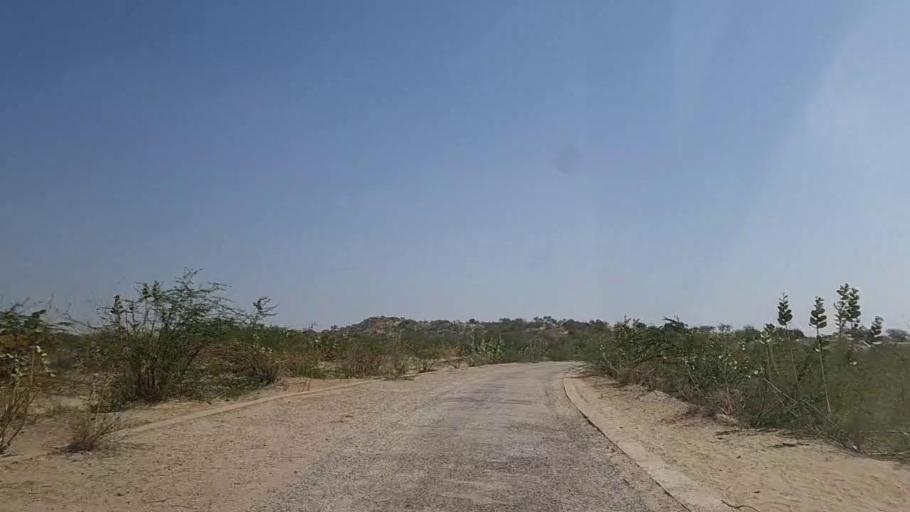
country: PK
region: Sindh
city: Diplo
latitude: 24.5139
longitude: 69.4172
